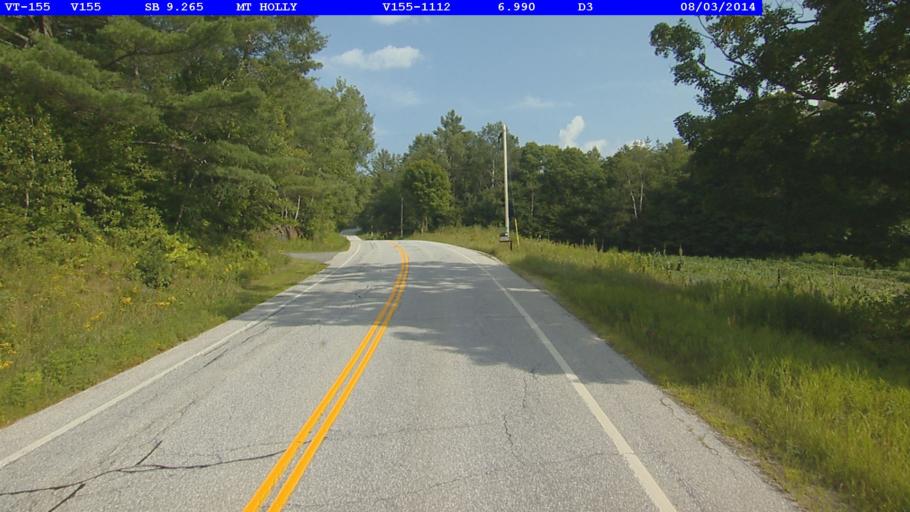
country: US
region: Vermont
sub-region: Rutland County
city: Rutland
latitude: 43.4412
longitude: -72.8656
